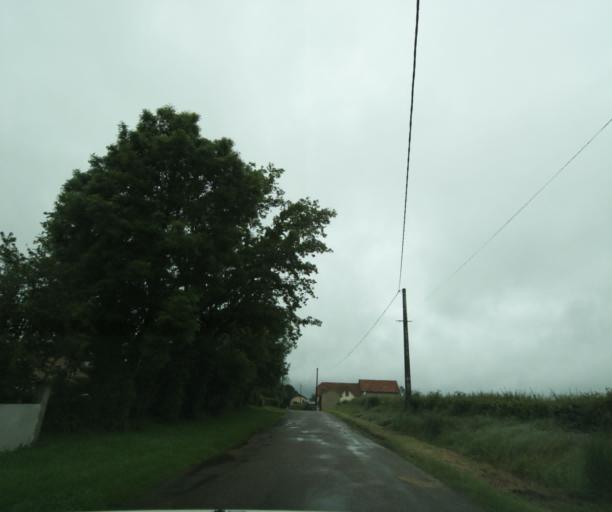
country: FR
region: Bourgogne
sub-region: Departement de Saone-et-Loire
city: Charolles
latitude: 46.4263
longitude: 4.2951
